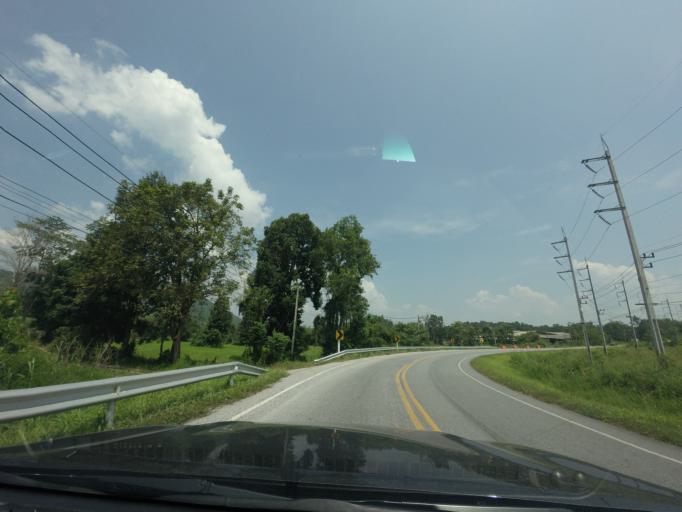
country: TH
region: Uttaradit
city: Thong Saen Khan
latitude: 17.4695
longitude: 100.2632
